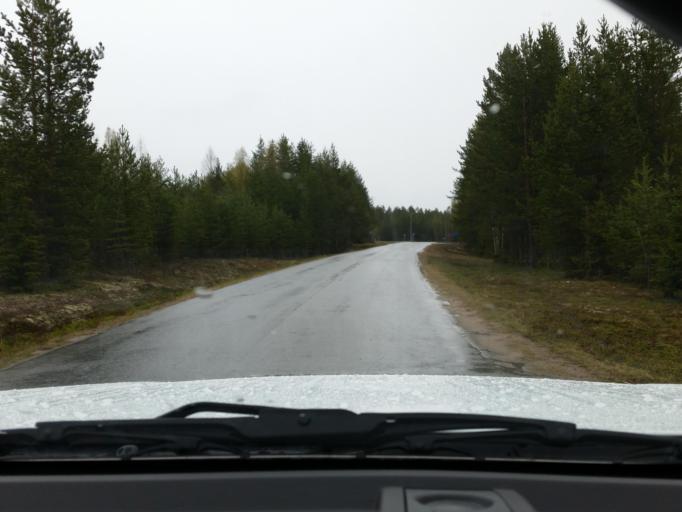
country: SE
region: Norrbotten
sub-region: Pitea Kommun
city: Rosvik
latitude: 65.4524
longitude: 21.6728
